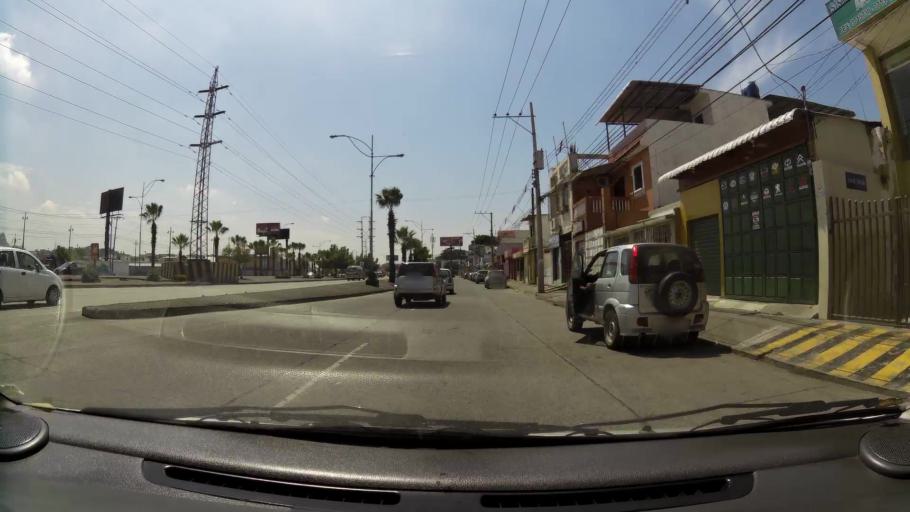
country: EC
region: Guayas
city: Eloy Alfaro
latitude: -2.1259
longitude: -79.9051
